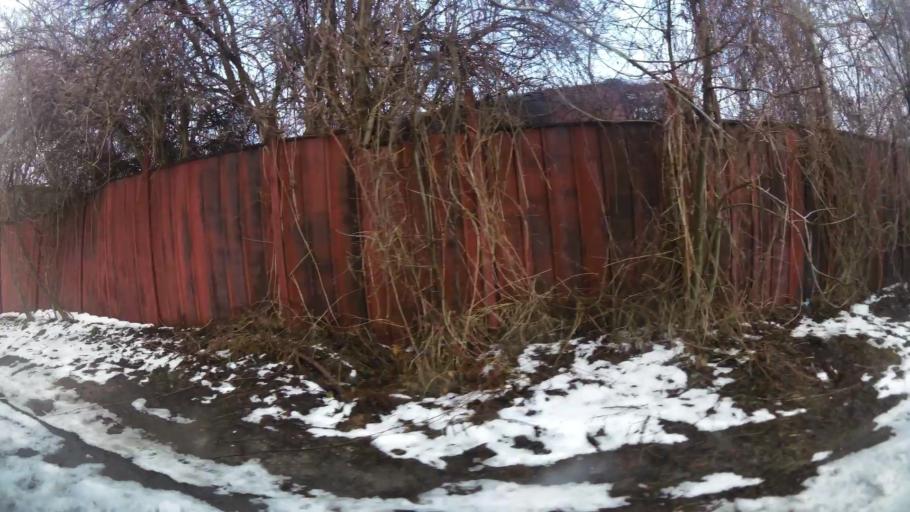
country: BG
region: Sofia-Capital
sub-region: Stolichna Obshtina
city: Sofia
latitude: 42.6506
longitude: 23.2631
